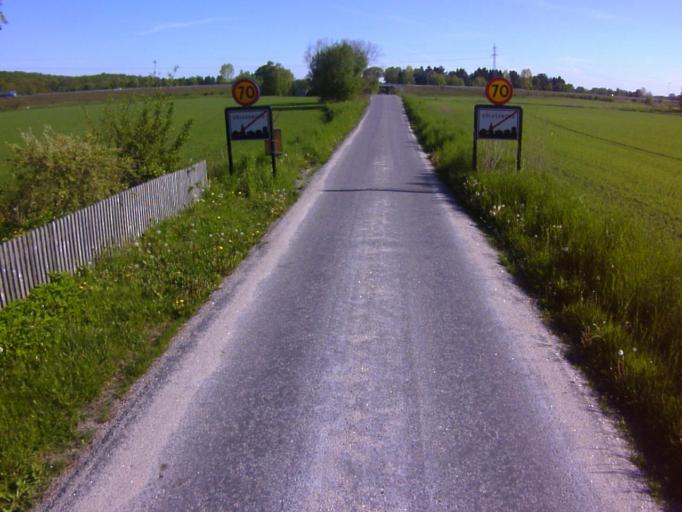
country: SE
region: Blekinge
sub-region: Solvesborgs Kommun
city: Soelvesborg
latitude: 56.0623
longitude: 14.6078
